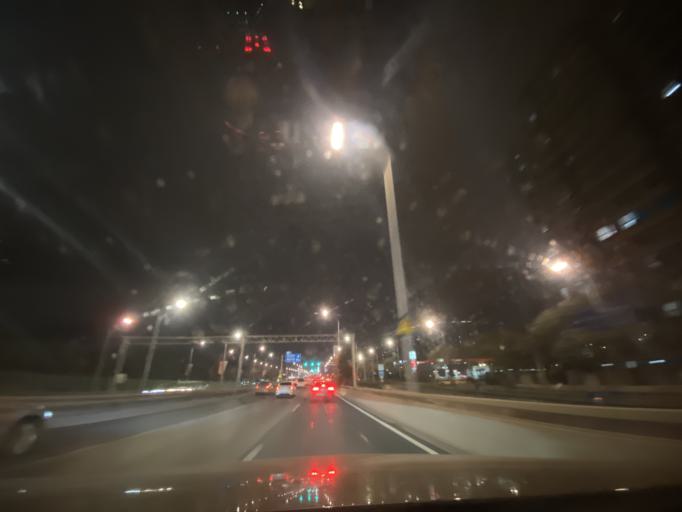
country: CN
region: Beijing
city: Babaoshan
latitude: 39.8958
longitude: 116.2440
